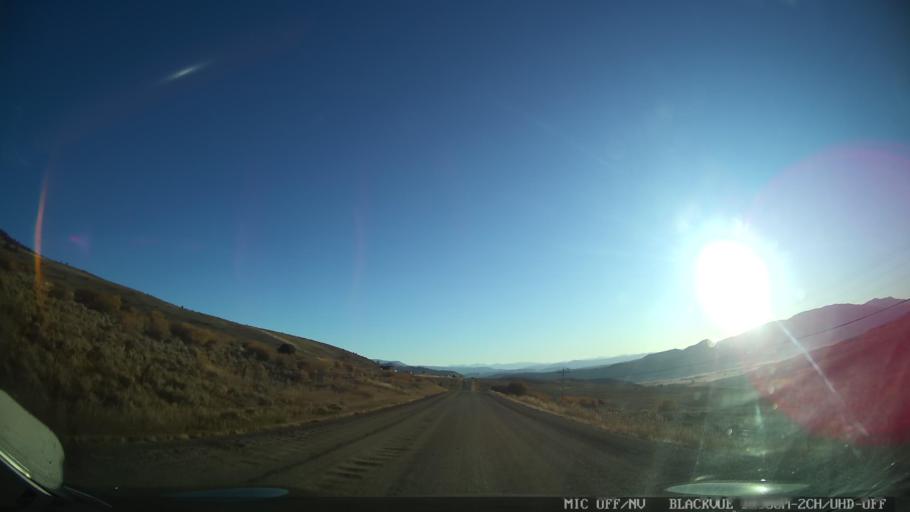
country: US
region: Colorado
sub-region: Grand County
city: Kremmling
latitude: 39.9896
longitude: -106.4244
